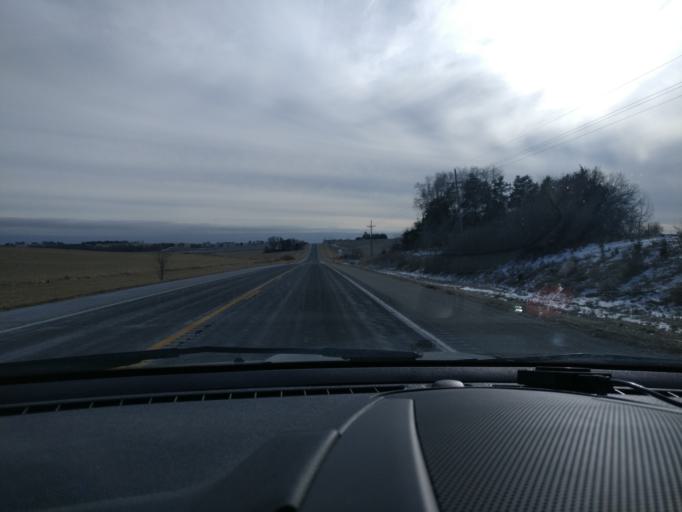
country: US
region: Nebraska
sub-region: Saunders County
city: Yutan
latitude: 41.3001
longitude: -96.5028
